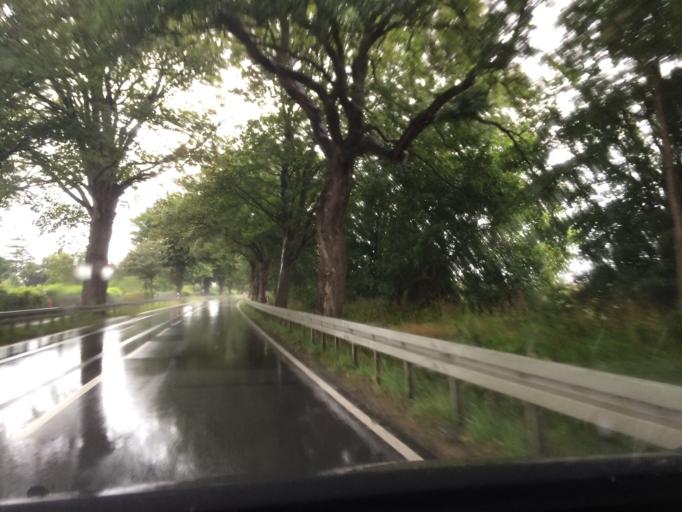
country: DE
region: Mecklenburg-Vorpommern
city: Kramerhof
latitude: 54.3370
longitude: 13.0589
